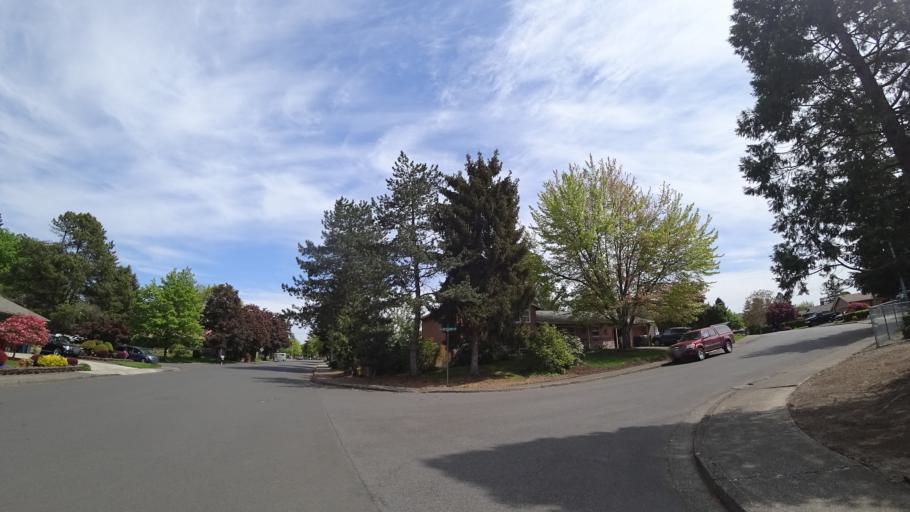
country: US
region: Oregon
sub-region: Washington County
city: Aloha
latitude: 45.4817
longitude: -122.8907
